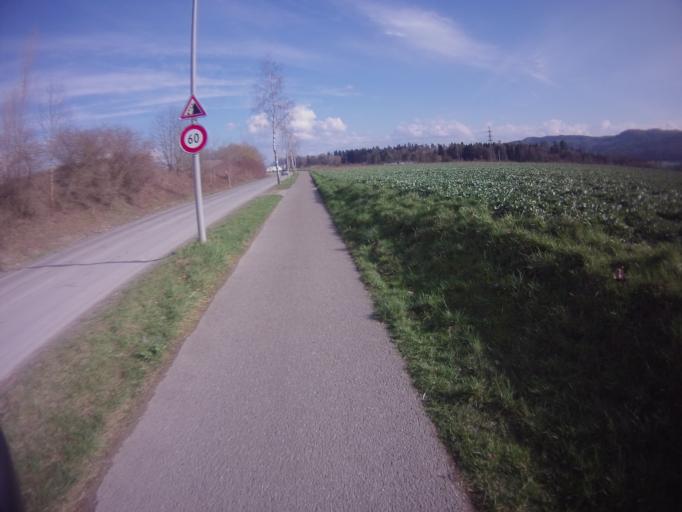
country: CH
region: Aargau
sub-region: Bezirk Baden
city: Neuenhof
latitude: 47.4532
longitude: 8.3404
